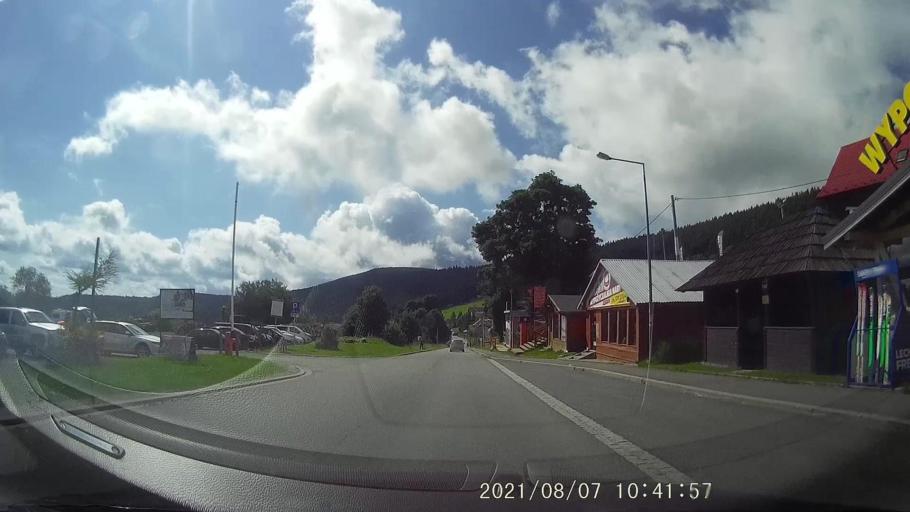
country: PL
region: Lower Silesian Voivodeship
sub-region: Powiat klodzki
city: Duszniki-Zdroj
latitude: 50.3351
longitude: 16.3890
